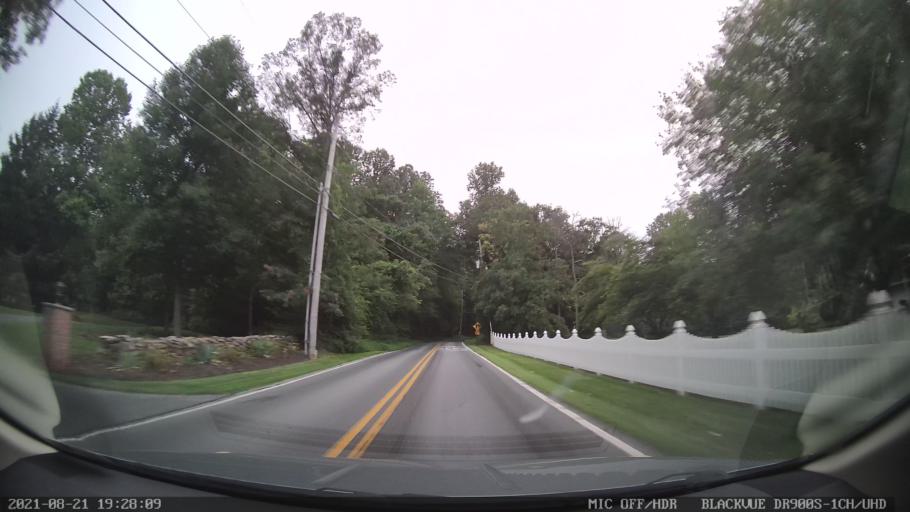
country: US
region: Pennsylvania
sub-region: Berks County
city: Oley
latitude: 40.4198
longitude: -75.7797
